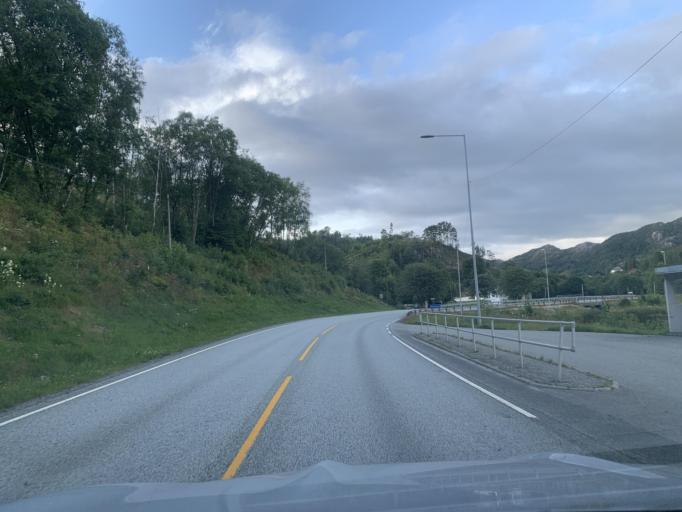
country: NO
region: Rogaland
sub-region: Bjerkreim
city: Vikesa
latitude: 58.5222
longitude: 6.0913
